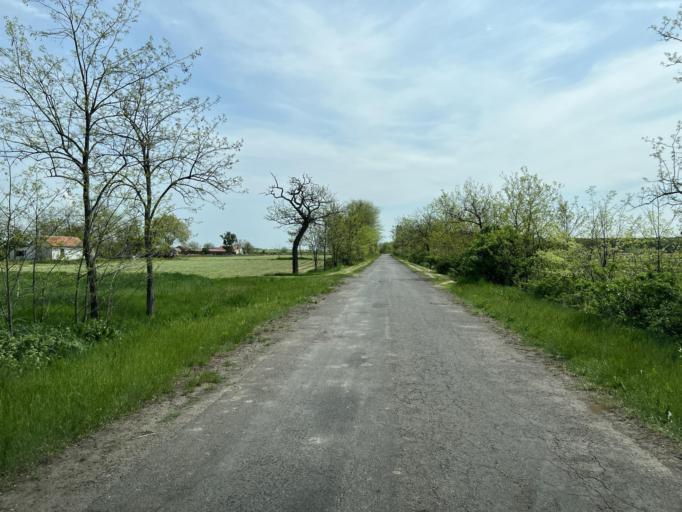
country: HU
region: Pest
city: Tapiogyorgye
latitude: 47.2909
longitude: 20.0040
